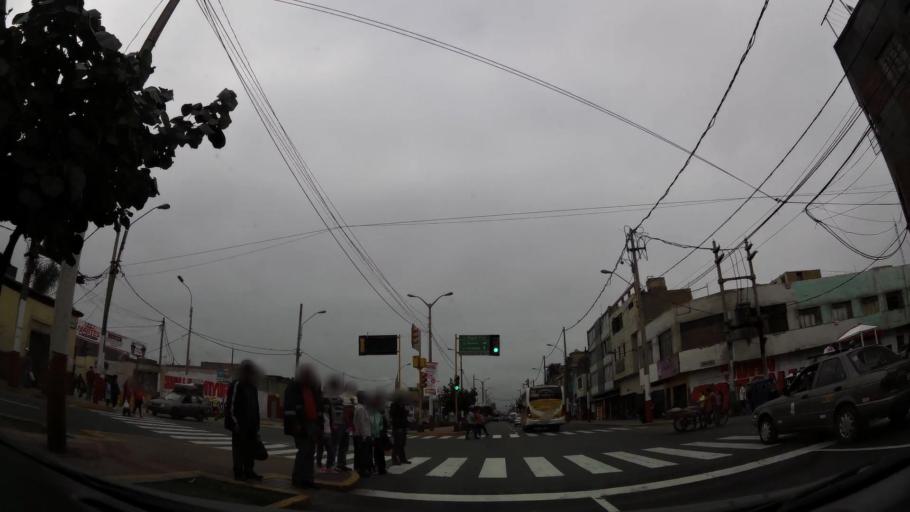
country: PE
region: Callao
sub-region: Callao
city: Callao
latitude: -12.0627
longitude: -77.1396
